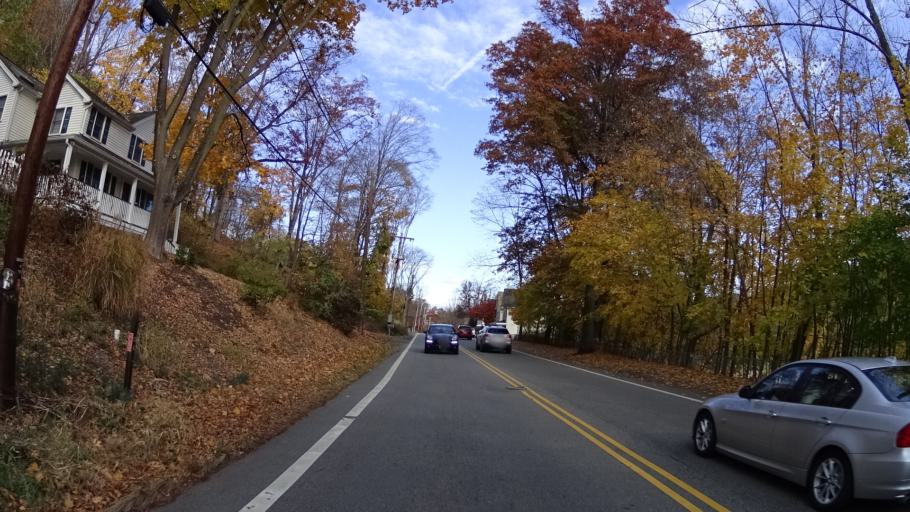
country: US
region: New Jersey
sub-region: Morris County
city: Morristown
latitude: 40.7990
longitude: -74.4985
